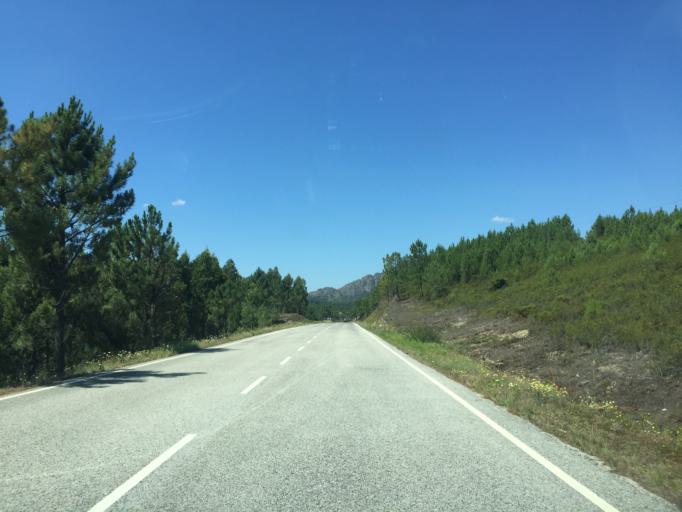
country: PT
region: Coimbra
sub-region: Pampilhosa da Serra
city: Pampilhosa da Serra
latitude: 40.1055
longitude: -7.8334
